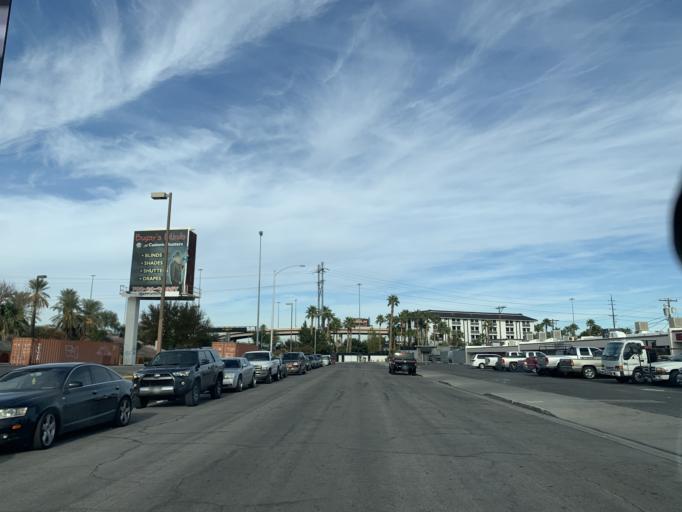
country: US
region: Nevada
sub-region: Clark County
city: Las Vegas
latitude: 36.1424
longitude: -115.1712
